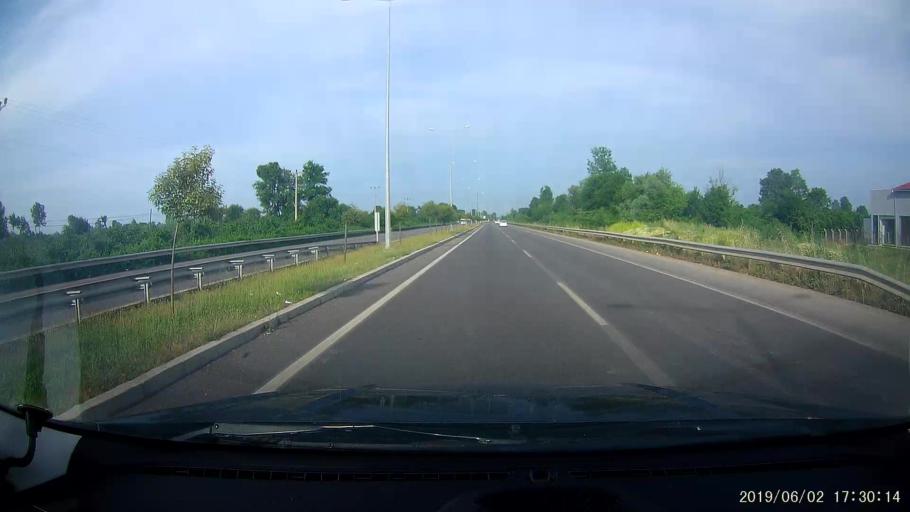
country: TR
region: Samsun
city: Carsamba
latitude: 41.2148
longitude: 36.7765
